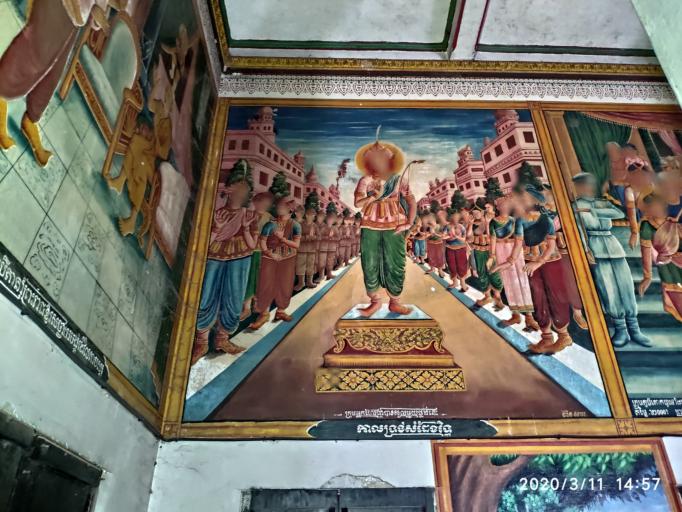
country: KH
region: Siem Reap
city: Siem Reap
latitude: 13.4137
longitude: 103.8645
